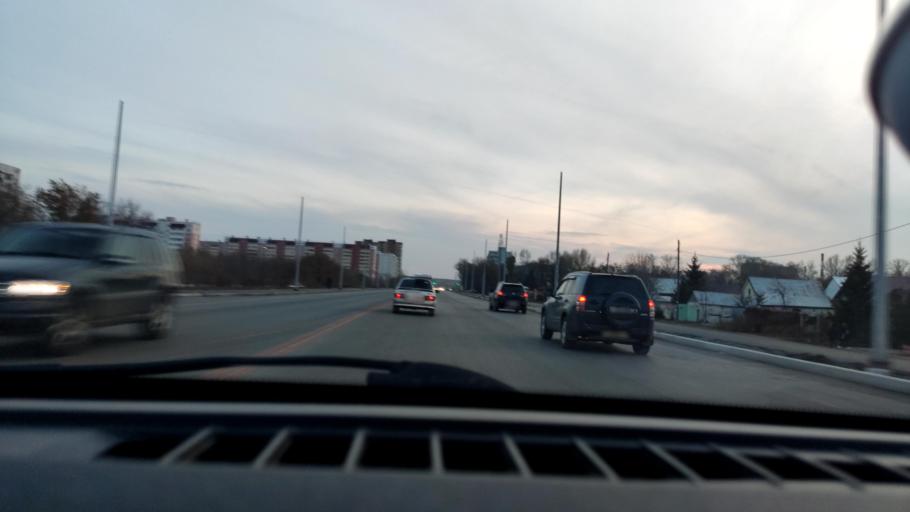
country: RU
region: Samara
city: Samara
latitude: 53.1144
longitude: 50.0840
